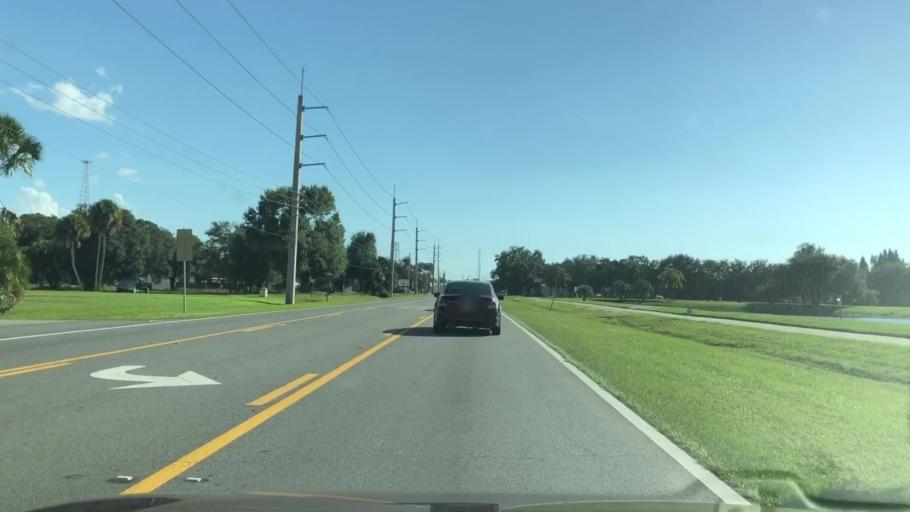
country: US
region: Florida
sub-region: Sarasota County
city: Fruitville
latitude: 27.3350
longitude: -82.4493
